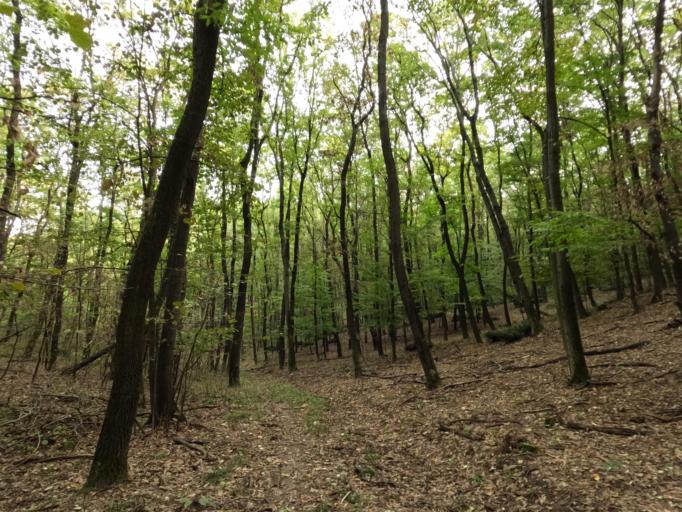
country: HU
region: Tolna
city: Szekszard
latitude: 46.3151
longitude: 18.6602
